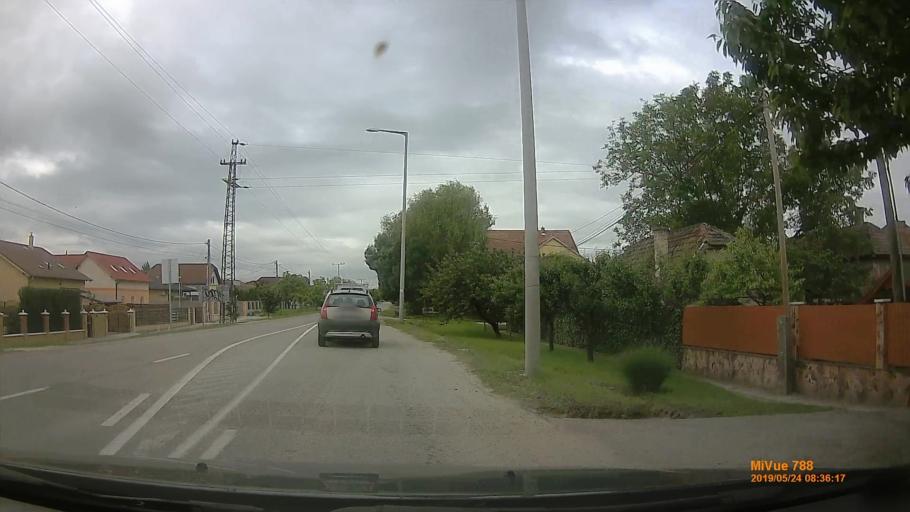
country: HU
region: Pest
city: Ullo
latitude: 47.3923
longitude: 19.3644
